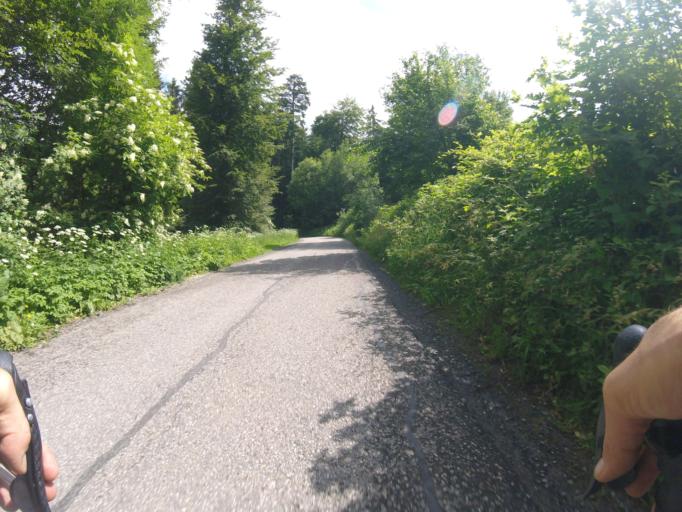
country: CH
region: Bern
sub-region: Bern-Mittelland District
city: Walkringen
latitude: 46.9687
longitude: 7.5984
